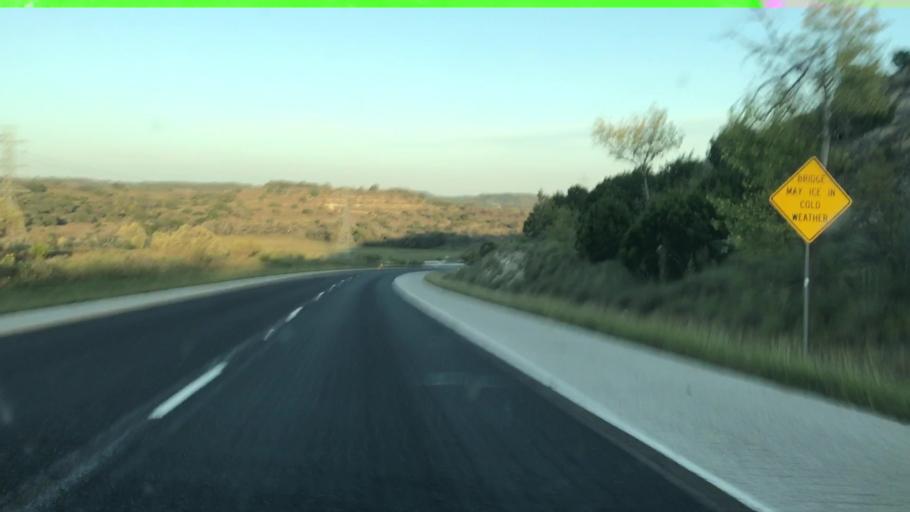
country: US
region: Texas
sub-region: Kerr County
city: Kerrville
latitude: 30.0529
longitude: -99.0157
